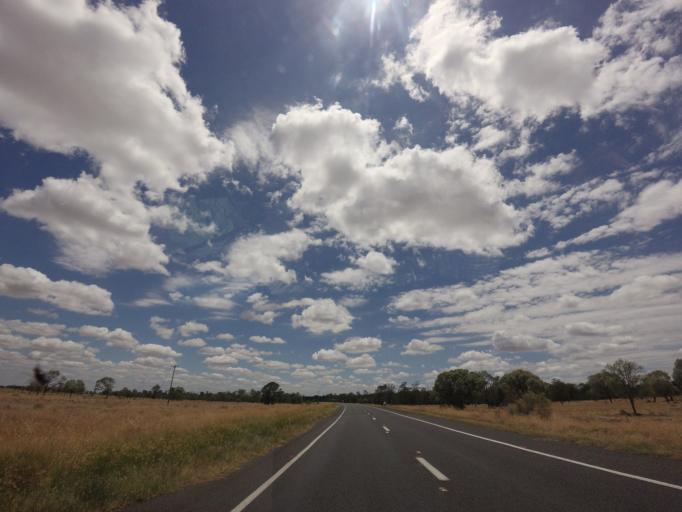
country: AU
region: New South Wales
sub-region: Moree Plains
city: Boggabilla
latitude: -28.9240
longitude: 150.1233
